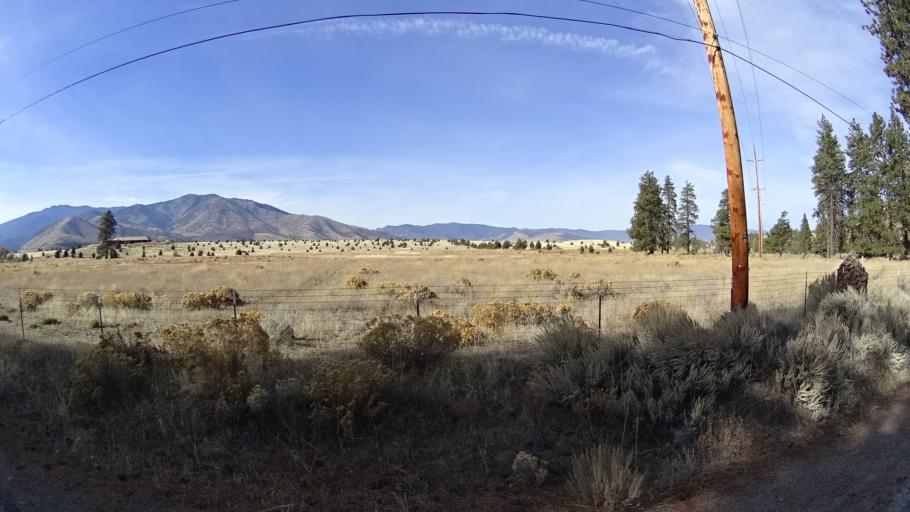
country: US
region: California
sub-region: Siskiyou County
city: Weed
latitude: 41.4865
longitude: -122.4433
